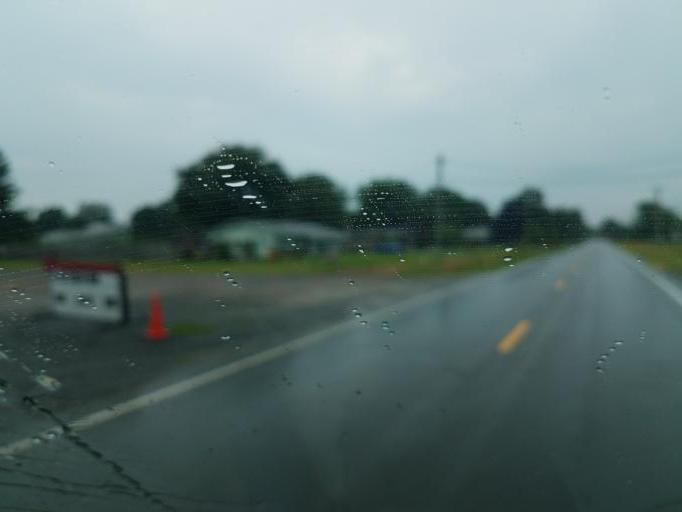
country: US
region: New York
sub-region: Niagara County
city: Ransomville
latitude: 43.2461
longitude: -78.9406
